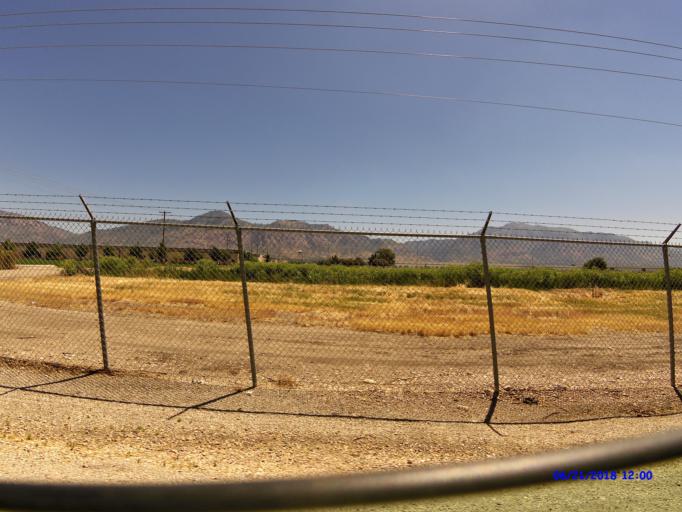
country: US
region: Utah
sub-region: Weber County
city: Marriott-Slaterville
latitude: 41.2581
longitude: -112.0090
